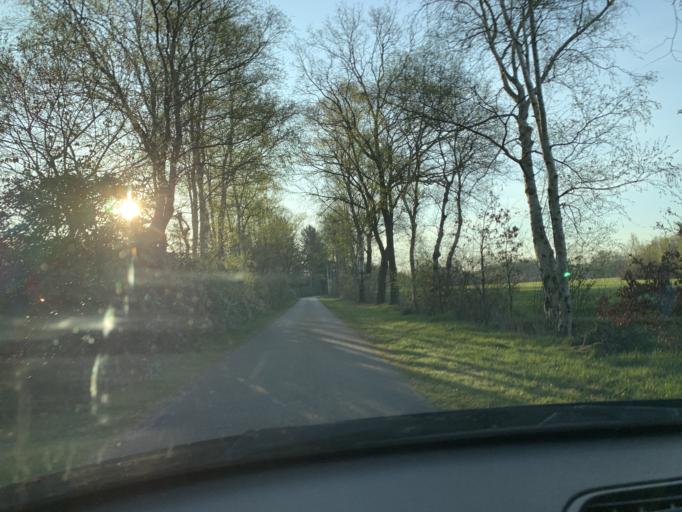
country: DE
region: Lower Saxony
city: Apen
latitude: 53.2876
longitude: 7.8214
